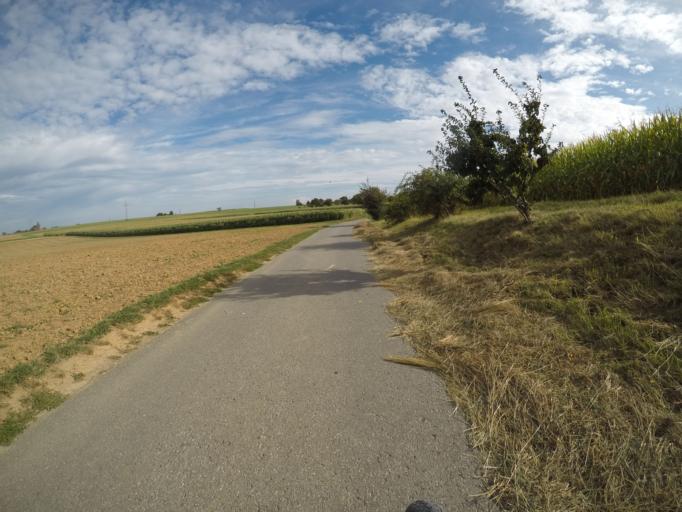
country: DE
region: Baden-Wuerttemberg
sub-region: Regierungsbezirk Stuttgart
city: Leonberg
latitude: 48.8308
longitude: 9.0030
